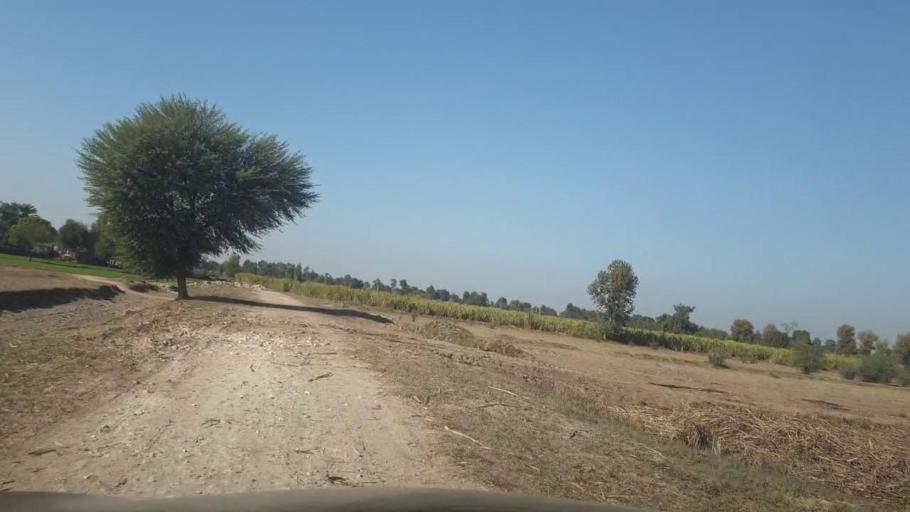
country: PK
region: Sindh
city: Mirpur Mathelo
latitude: 28.1454
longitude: 69.5920
